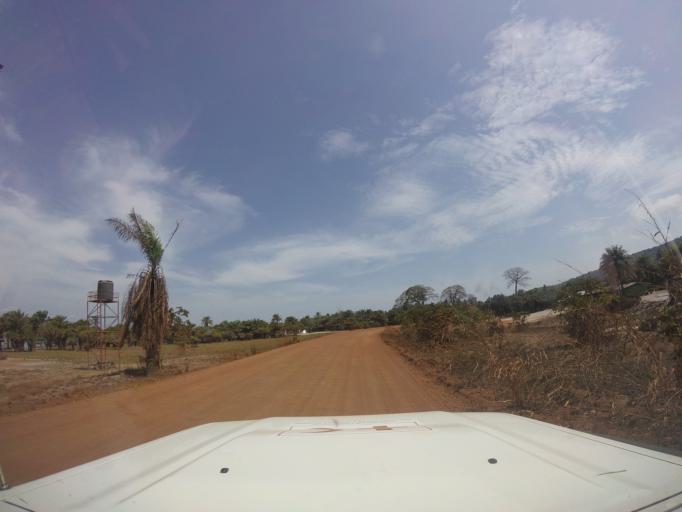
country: LR
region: Grand Cape Mount
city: Robertsport
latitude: 6.7441
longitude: -11.3382
